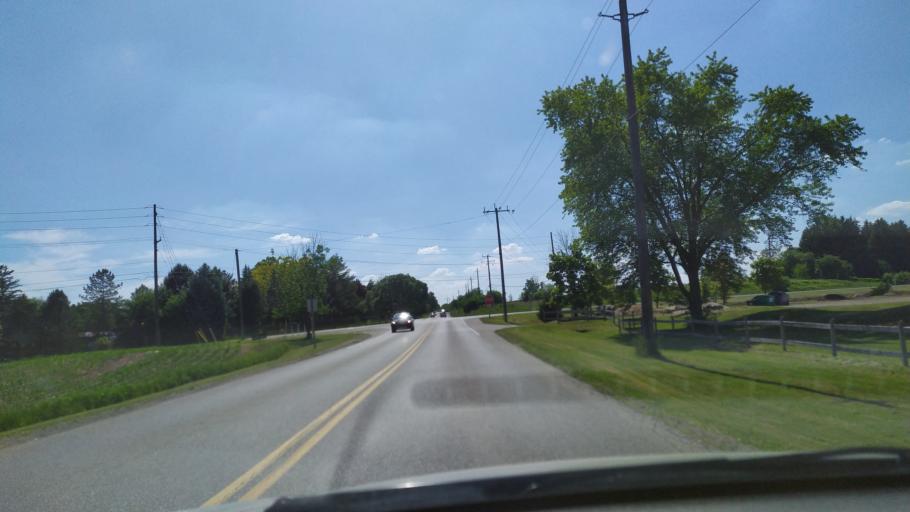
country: CA
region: Ontario
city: Kitchener
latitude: 43.3715
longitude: -80.5583
